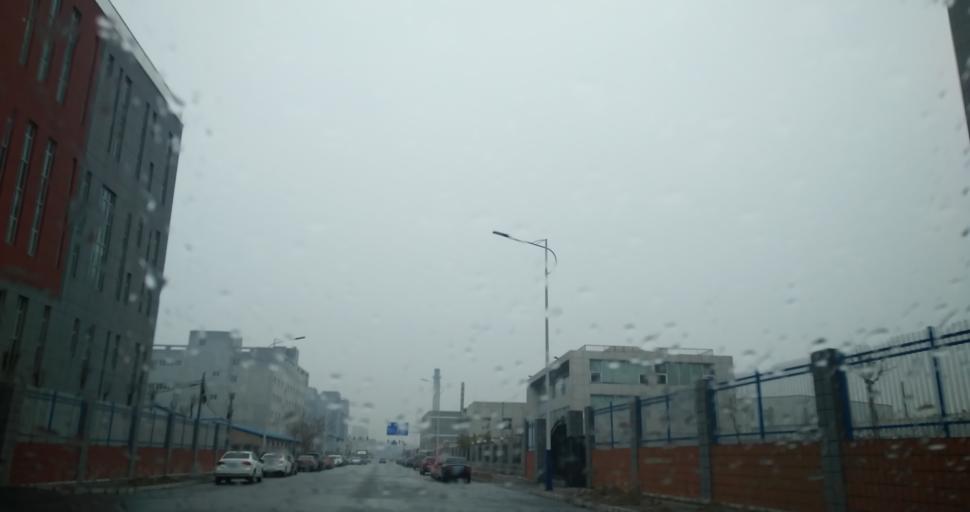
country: CN
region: Beijing
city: Yinghai
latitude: 39.7111
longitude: 116.4136
